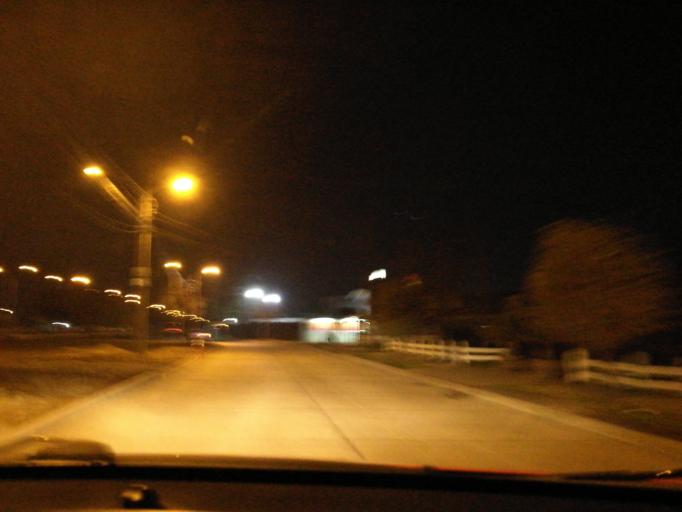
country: CL
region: O'Higgins
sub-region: Provincia de Cachapoal
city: Rancagua
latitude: -34.1651
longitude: -70.7269
